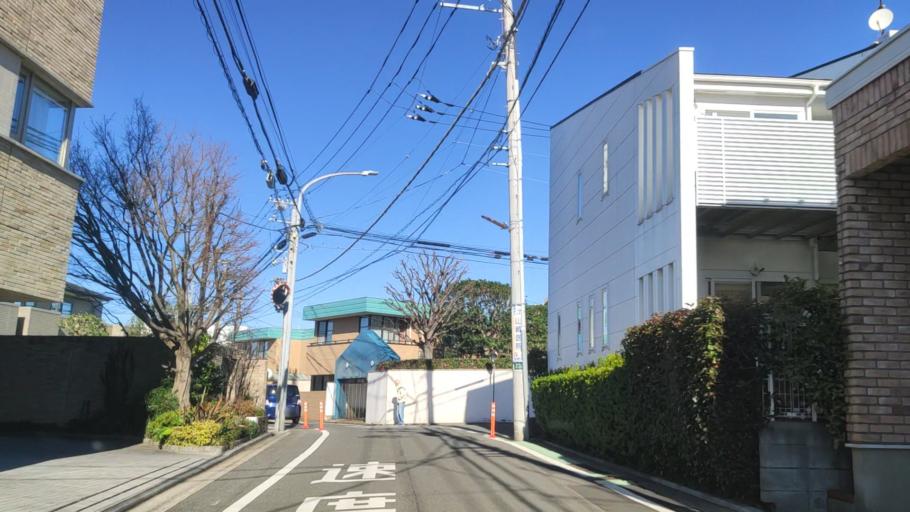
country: JP
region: Kanagawa
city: Yokohama
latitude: 35.4258
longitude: 139.6417
